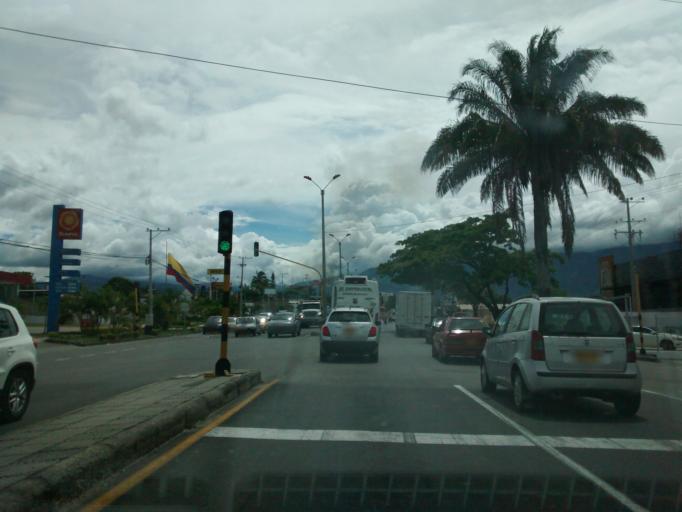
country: CO
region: Tolima
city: Ibague
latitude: 4.4072
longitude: -75.1659
